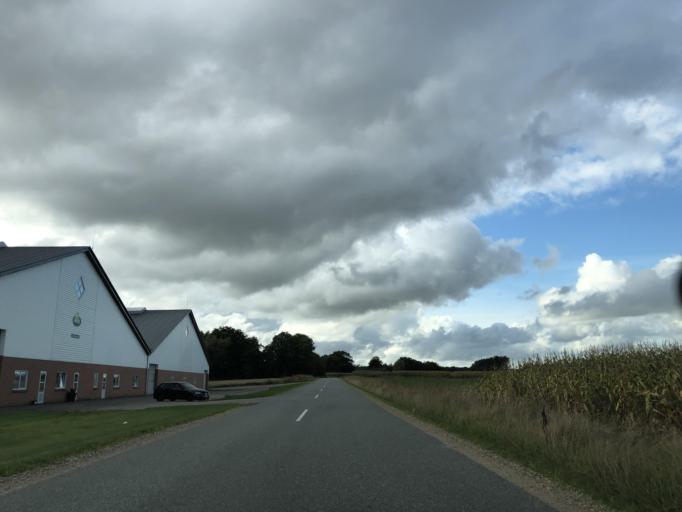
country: DK
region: South Denmark
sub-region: Varde Kommune
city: Olgod
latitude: 55.7596
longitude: 8.6344
